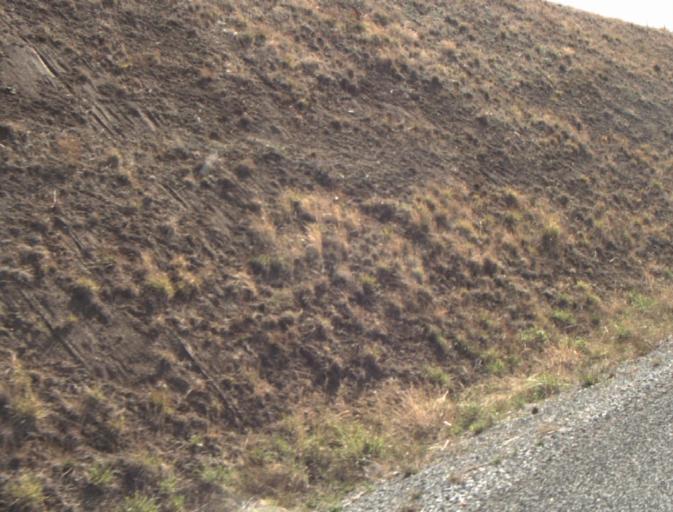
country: AU
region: Tasmania
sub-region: Launceston
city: Mayfield
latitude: -41.3569
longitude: 147.1053
